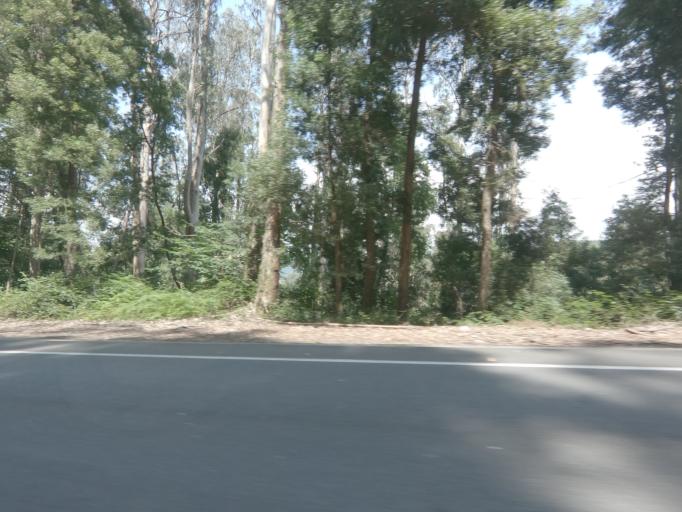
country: ES
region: Galicia
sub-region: Provincia de Pontevedra
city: Gondomar
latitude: 42.0930
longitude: -8.7548
